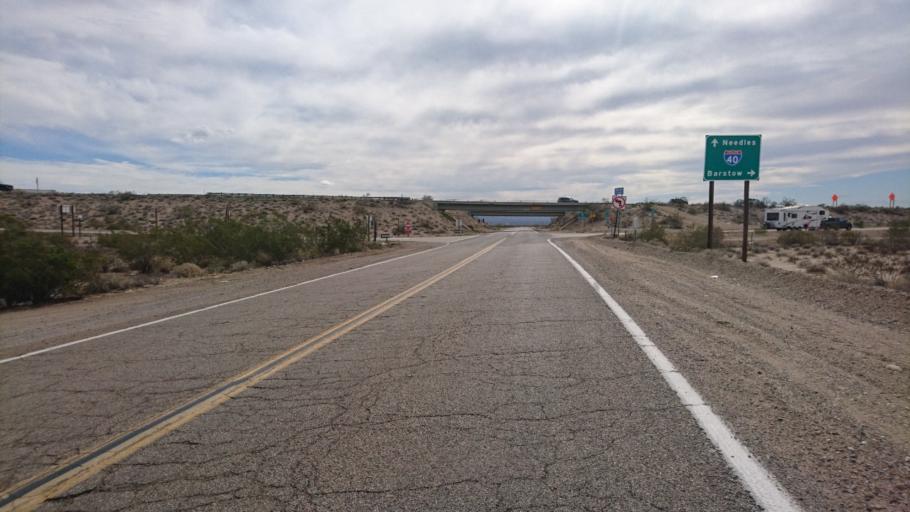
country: US
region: California
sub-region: San Bernardino County
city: Needles
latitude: 34.8137
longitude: -115.1900
